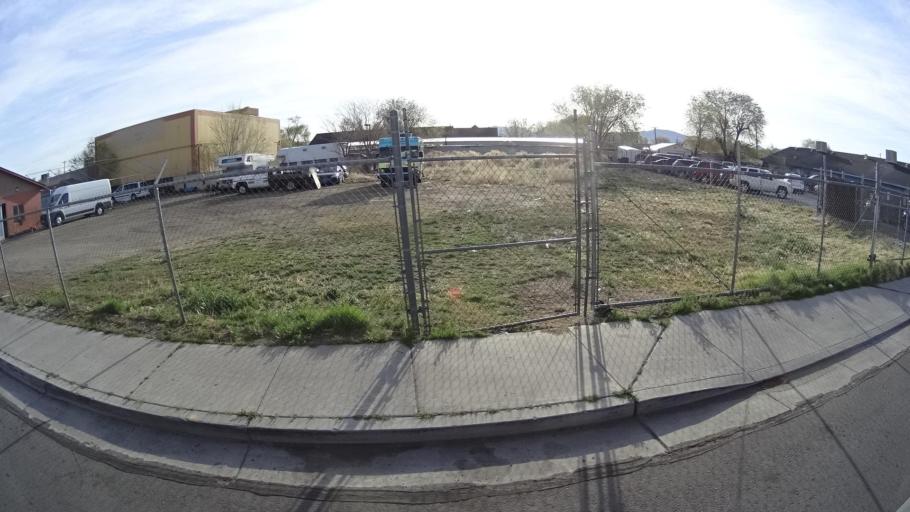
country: US
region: Nevada
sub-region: Washoe County
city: Reno
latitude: 39.4987
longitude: -119.7963
